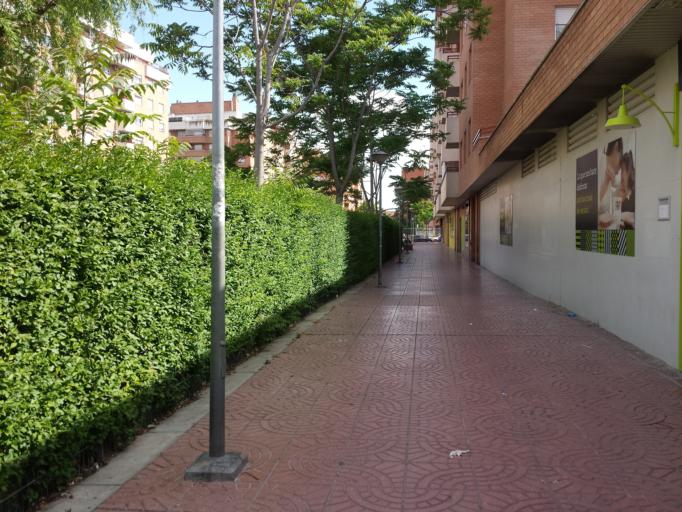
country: ES
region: Aragon
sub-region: Provincia de Zaragoza
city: Zaragoza
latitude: 41.6718
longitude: -0.8764
